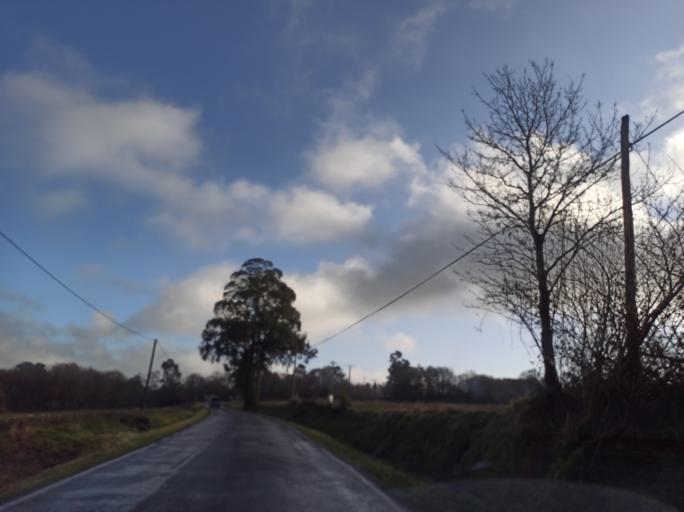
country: ES
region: Galicia
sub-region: Provincia da Coruna
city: Curtis
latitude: 43.0970
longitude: -7.9868
